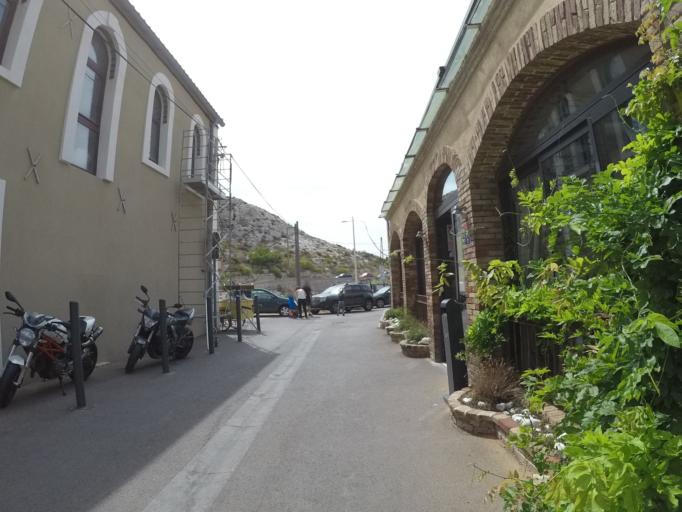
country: FR
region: Provence-Alpes-Cote d'Azur
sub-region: Departement des Bouches-du-Rhone
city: Marseille 08
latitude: 43.2128
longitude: 5.3543
